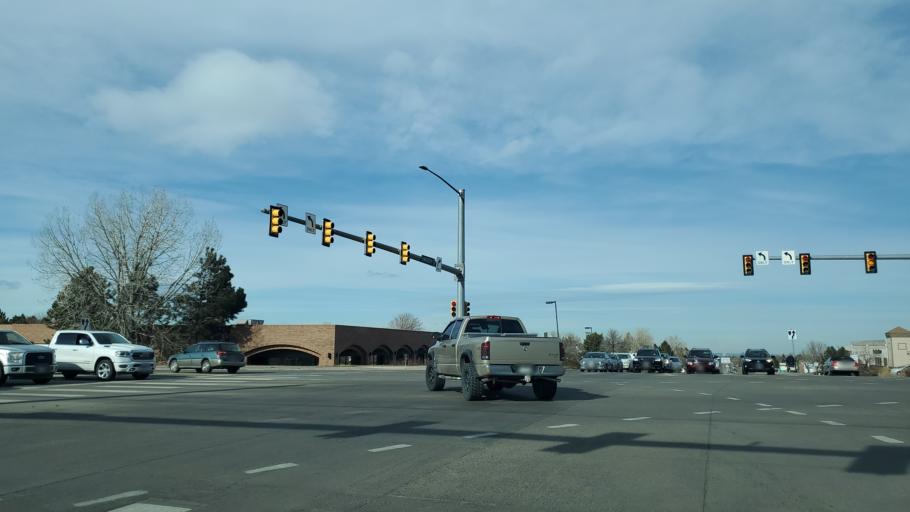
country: US
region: Colorado
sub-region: Douglas County
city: Highlands Ranch
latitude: 39.5659
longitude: -104.9605
